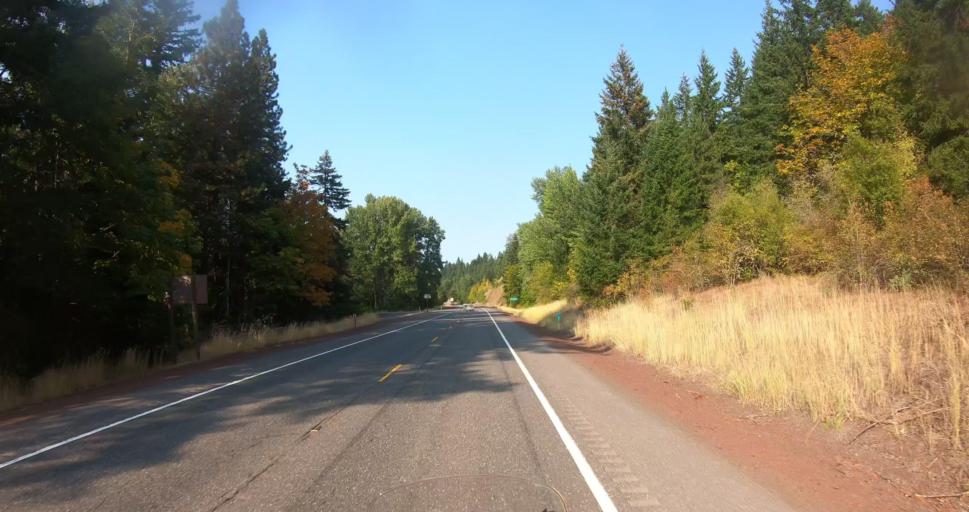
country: US
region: Oregon
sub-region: Hood River County
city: Odell
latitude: 45.4962
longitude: -121.5628
